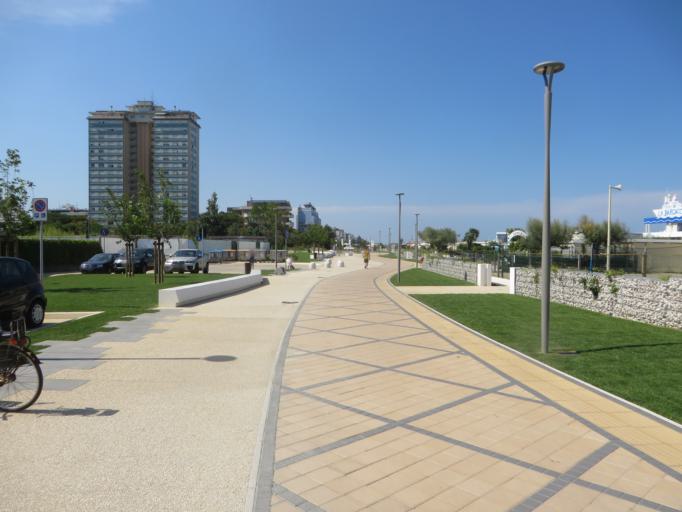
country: IT
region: Emilia-Romagna
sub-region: Provincia di Ravenna
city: Cervia
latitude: 44.2764
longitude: 12.3532
